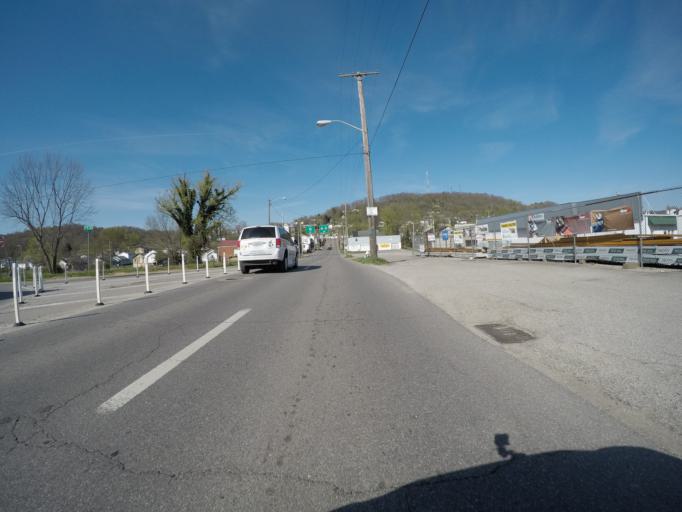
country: US
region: West Virginia
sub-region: Kanawha County
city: South Charleston
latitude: 38.3706
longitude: -81.6655
